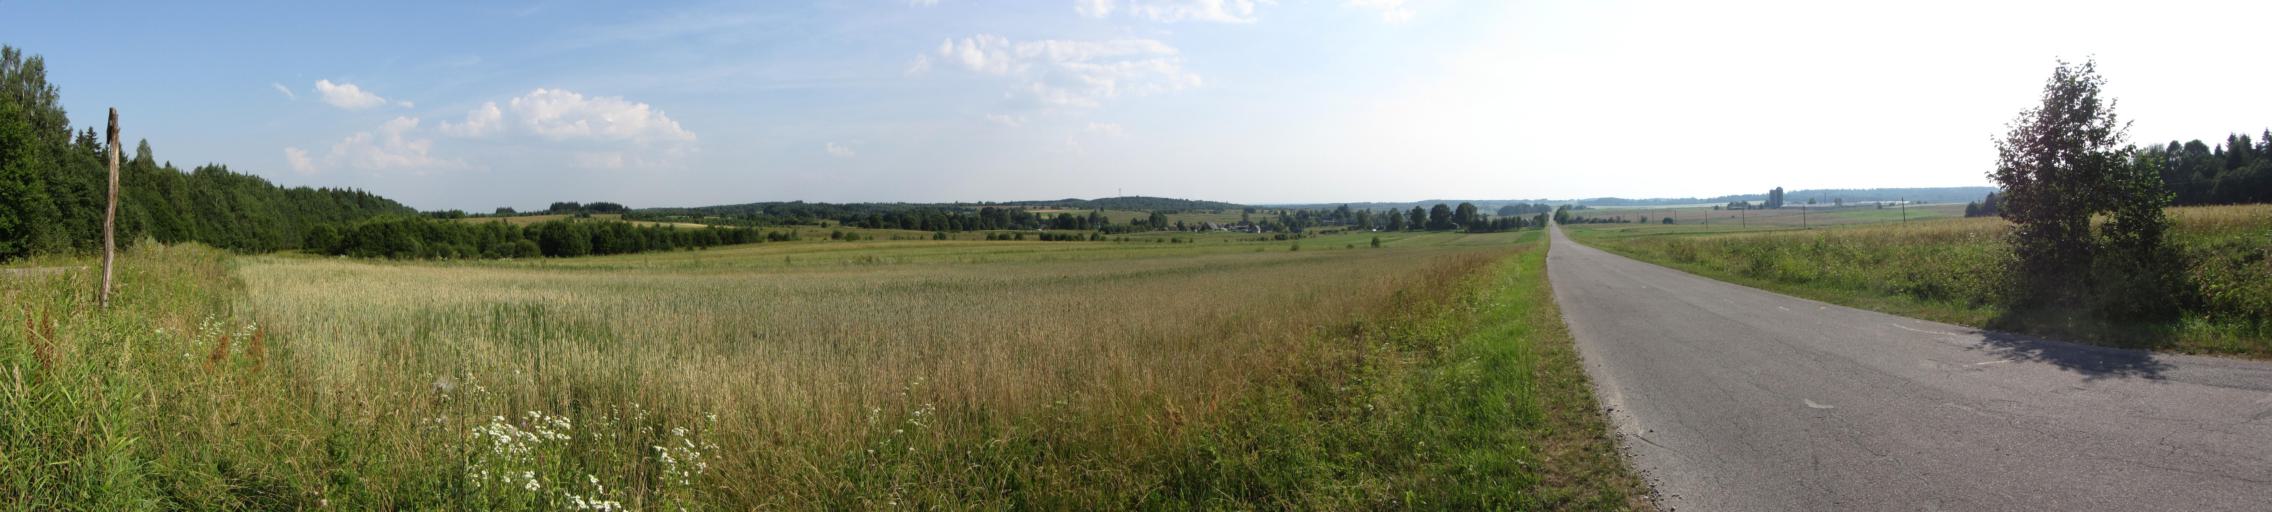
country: LT
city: Skaidiskes
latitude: 54.5238
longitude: 25.6347
